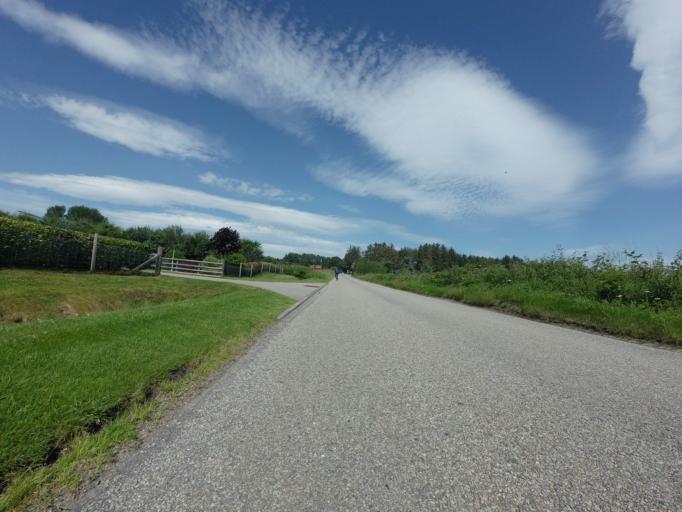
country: GB
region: Scotland
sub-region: Highland
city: Inverness
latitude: 57.5296
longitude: -4.3199
